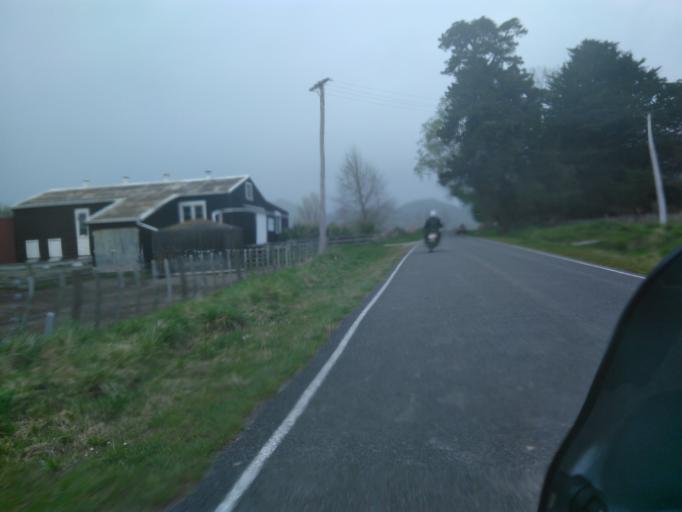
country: NZ
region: Gisborne
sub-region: Gisborne District
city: Gisborne
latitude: -38.6524
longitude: 177.7257
